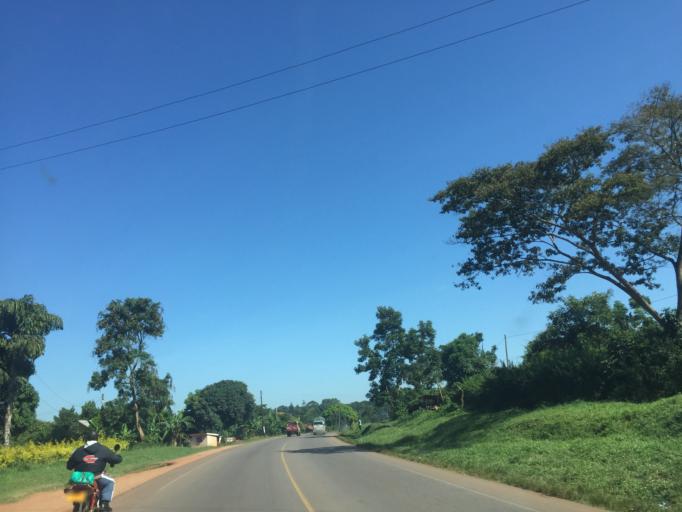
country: UG
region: Central Region
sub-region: Luwero District
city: Wobulenzi
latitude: 0.7404
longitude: 32.5173
